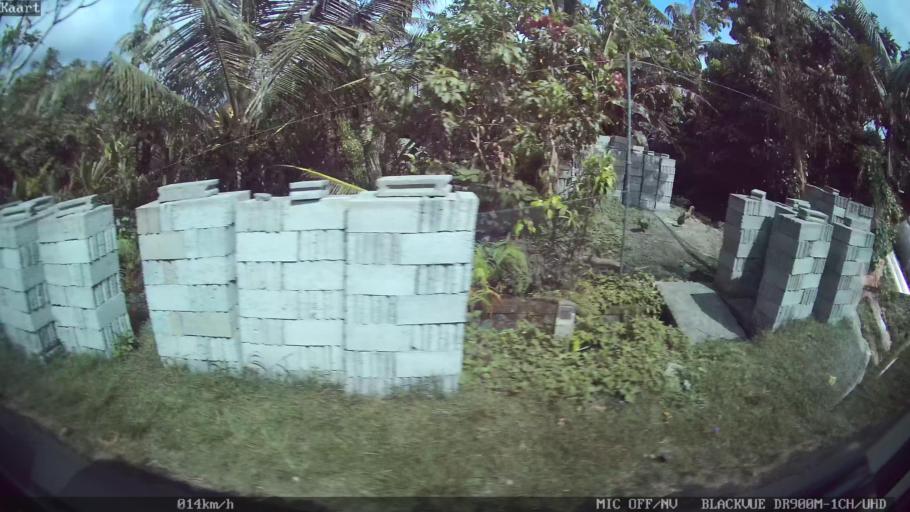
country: ID
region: Bali
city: Banjar Batur
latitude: -8.5966
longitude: 115.2109
